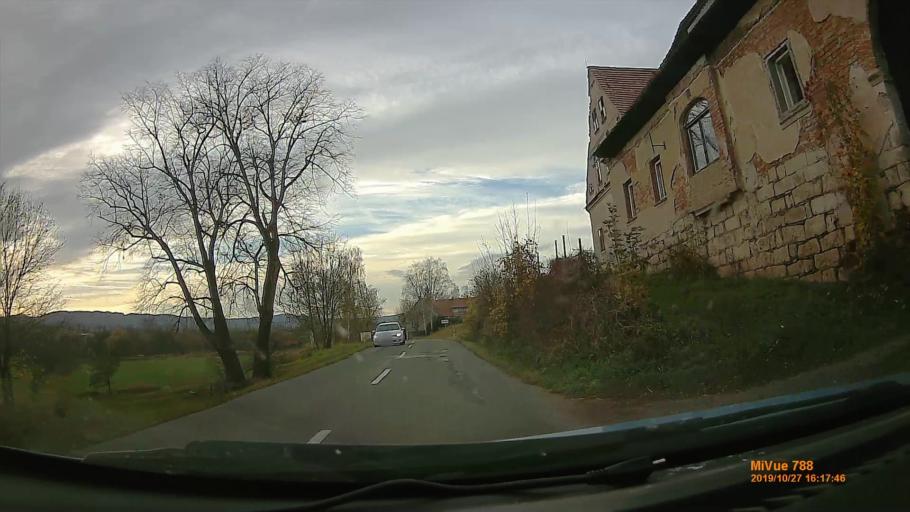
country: CZ
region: Kralovehradecky
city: Broumov
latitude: 50.5645
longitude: 16.3611
